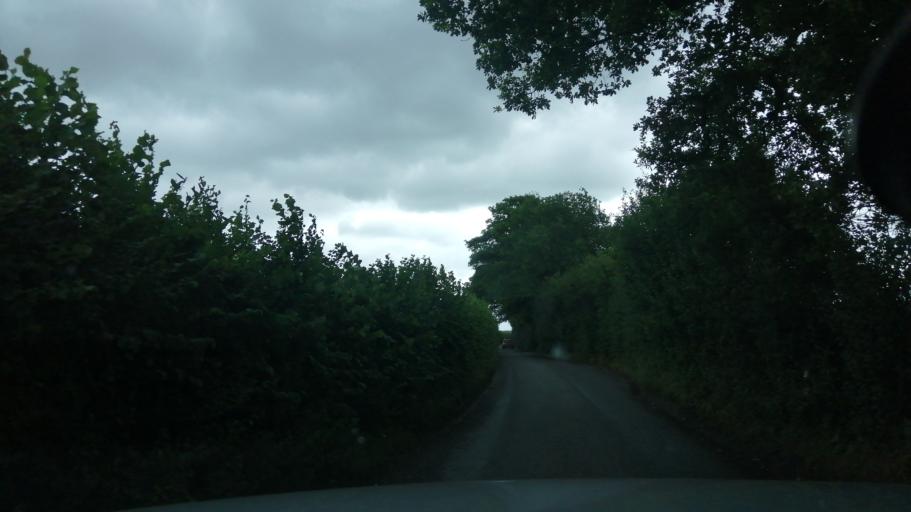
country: GB
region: England
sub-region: Herefordshire
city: Madley
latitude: 52.0253
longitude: -2.8593
